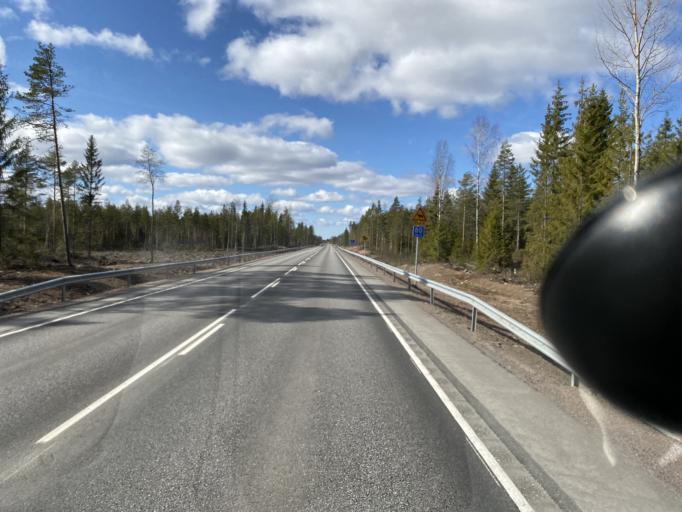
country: FI
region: Satakunta
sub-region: Pori
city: Kokemaeki
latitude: 61.1667
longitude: 22.4234
